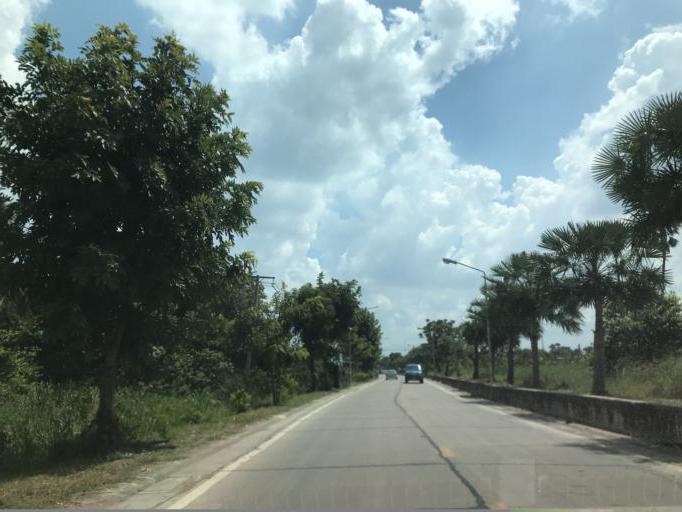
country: TH
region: Pathum Thani
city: Pathum Thani
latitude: 14.0084
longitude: 100.5415
